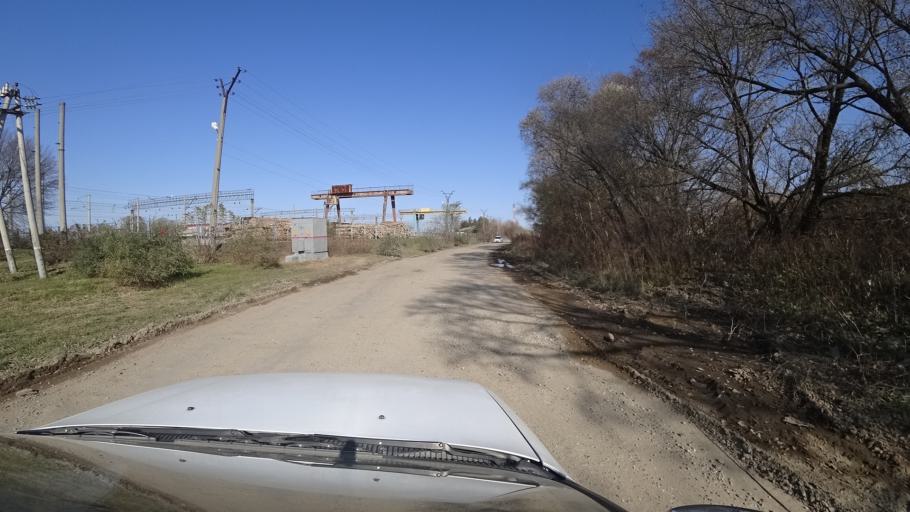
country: RU
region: Primorskiy
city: Dal'nerechensk
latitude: 45.9329
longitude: 133.7188
